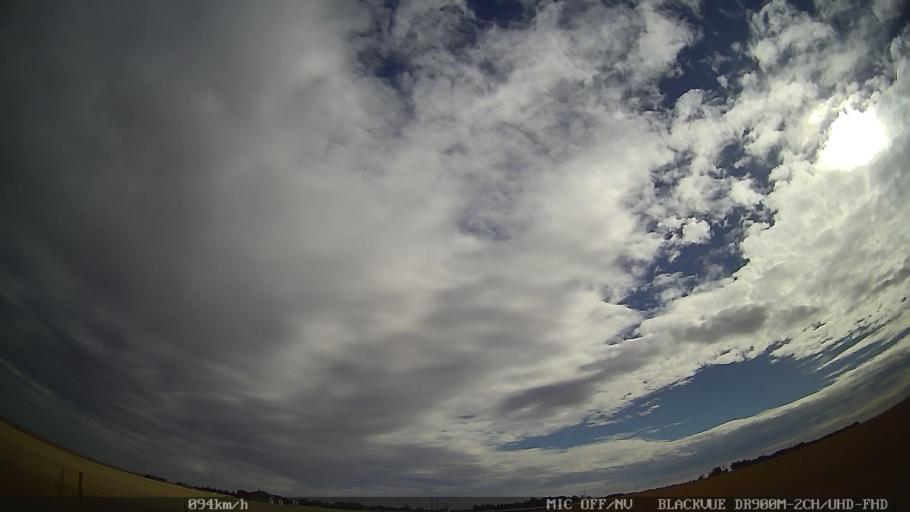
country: US
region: New Mexico
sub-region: Curry County
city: Texico
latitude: 34.4193
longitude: -103.1113
